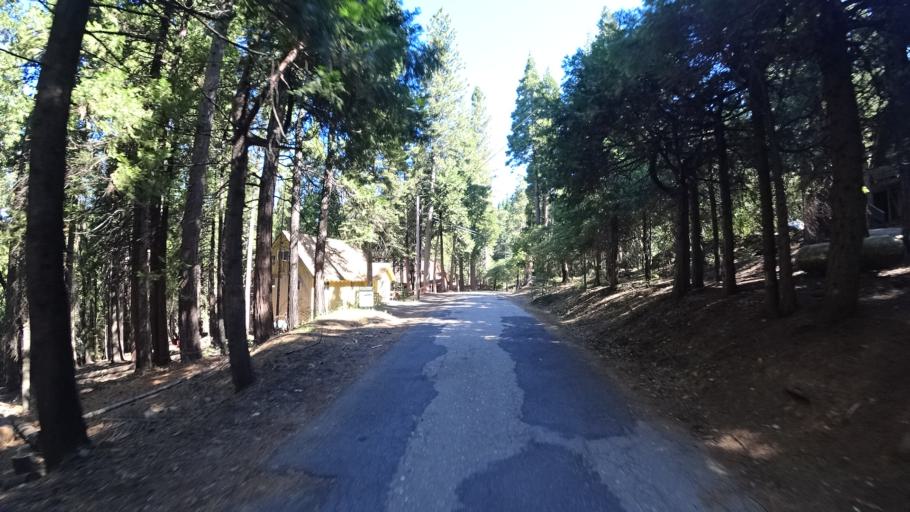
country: US
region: California
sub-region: Calaveras County
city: Arnold
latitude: 38.2985
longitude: -120.2717
